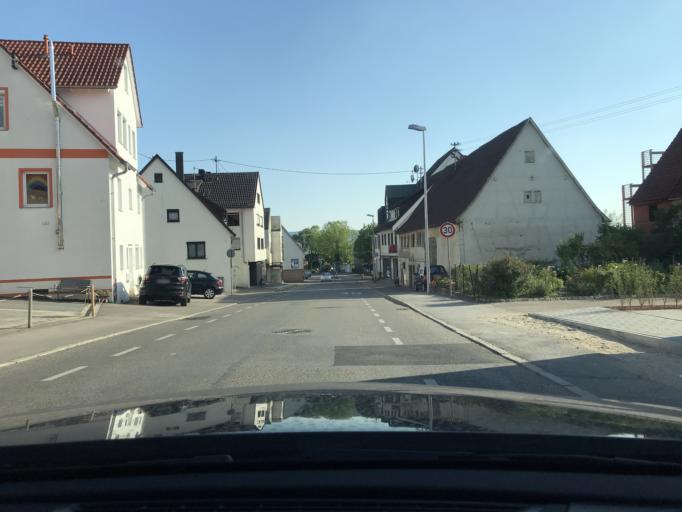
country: DE
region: Baden-Wuerttemberg
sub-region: Regierungsbezirk Stuttgart
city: Waiblingen
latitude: 48.8492
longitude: 9.3221
